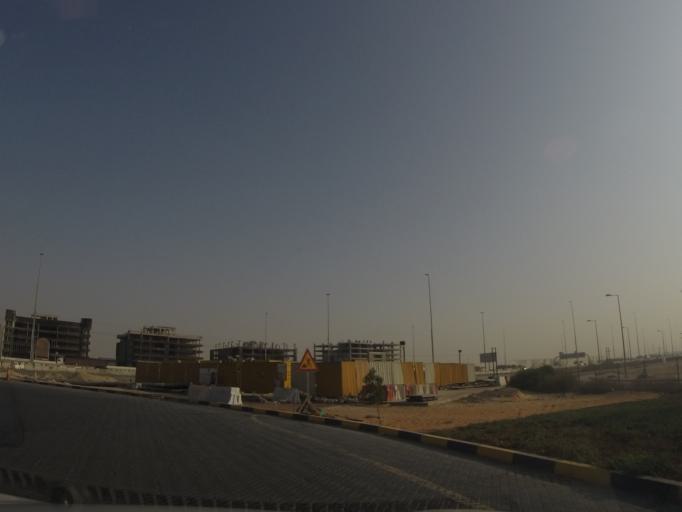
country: AE
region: Dubai
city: Dubai
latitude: 25.0323
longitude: 55.1740
